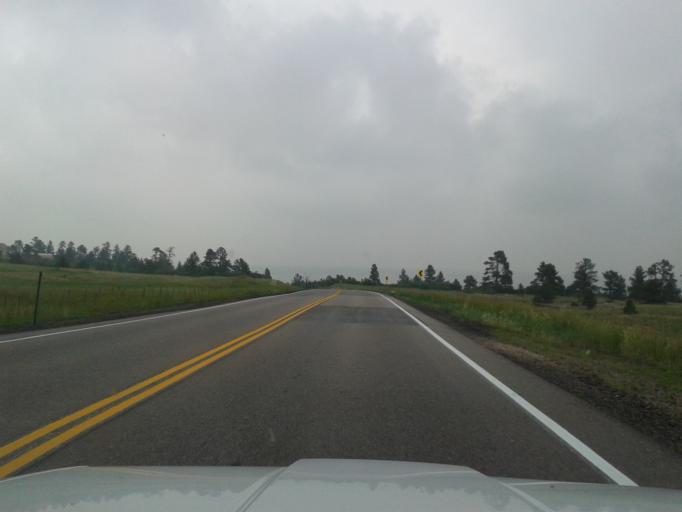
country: US
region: Colorado
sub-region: Elbert County
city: Ponderosa Park
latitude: 39.3434
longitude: -104.7337
